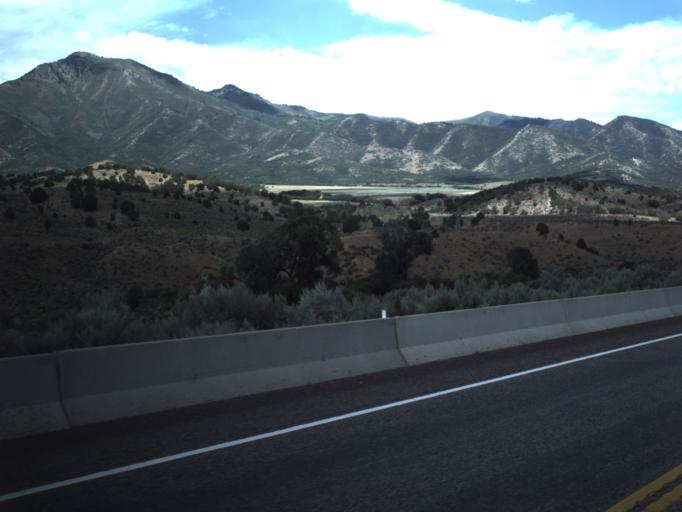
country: US
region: Utah
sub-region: Utah County
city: Woodland Hills
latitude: 39.9345
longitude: -111.5439
